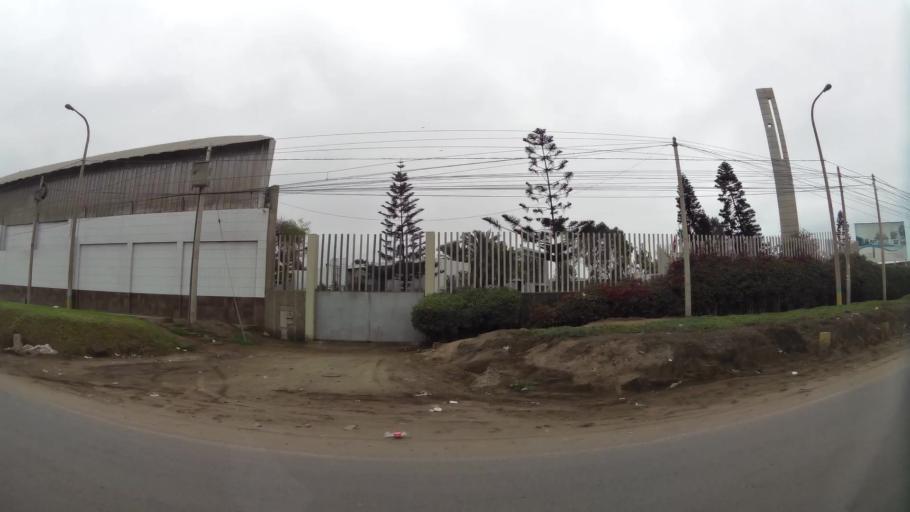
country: PE
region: Lima
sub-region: Lima
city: Surco
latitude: -12.2202
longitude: -76.9756
